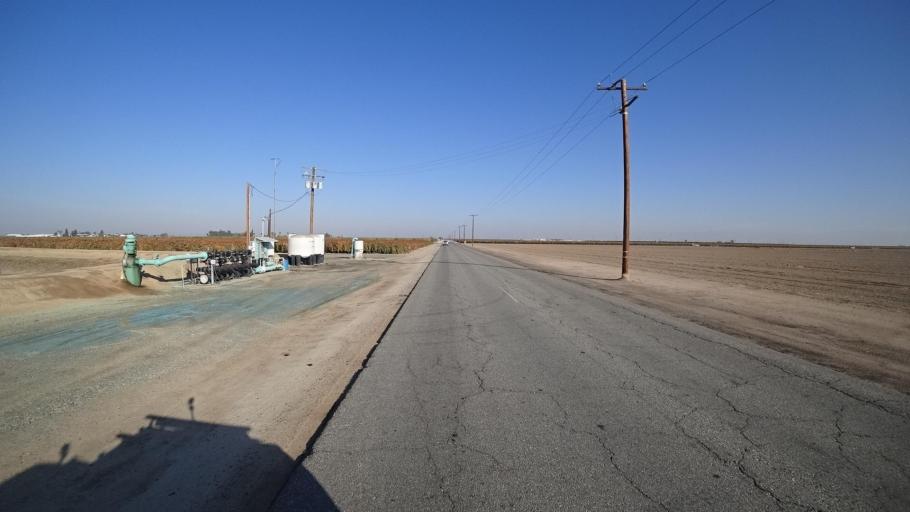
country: US
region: California
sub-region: Tulare County
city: Richgrove
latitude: 35.7666
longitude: -119.1697
